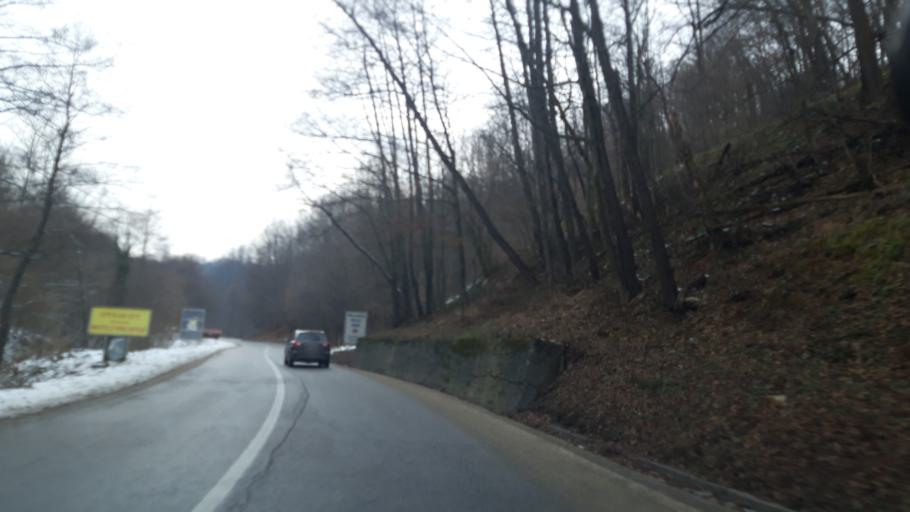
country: BA
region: Republika Srpska
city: Vlasenica
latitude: 44.1809
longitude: 19.0091
